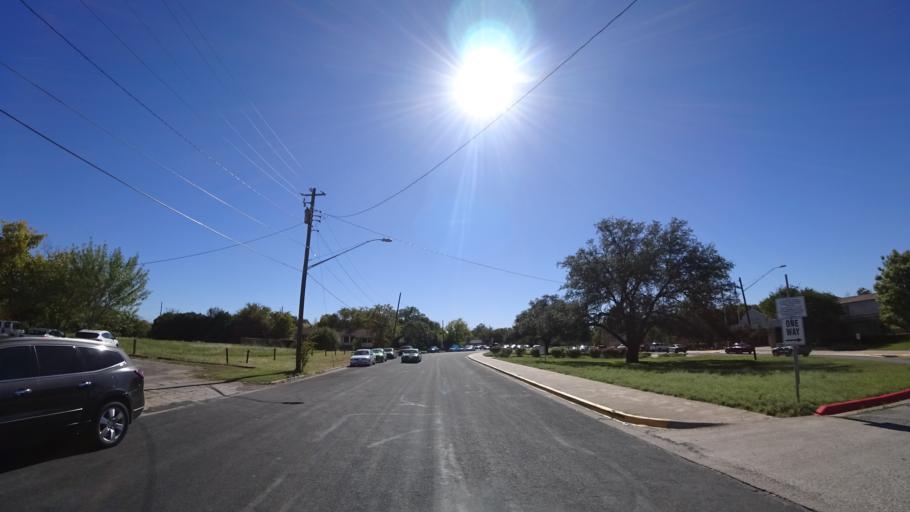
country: US
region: Texas
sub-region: Travis County
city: Austin
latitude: 30.3258
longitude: -97.7294
